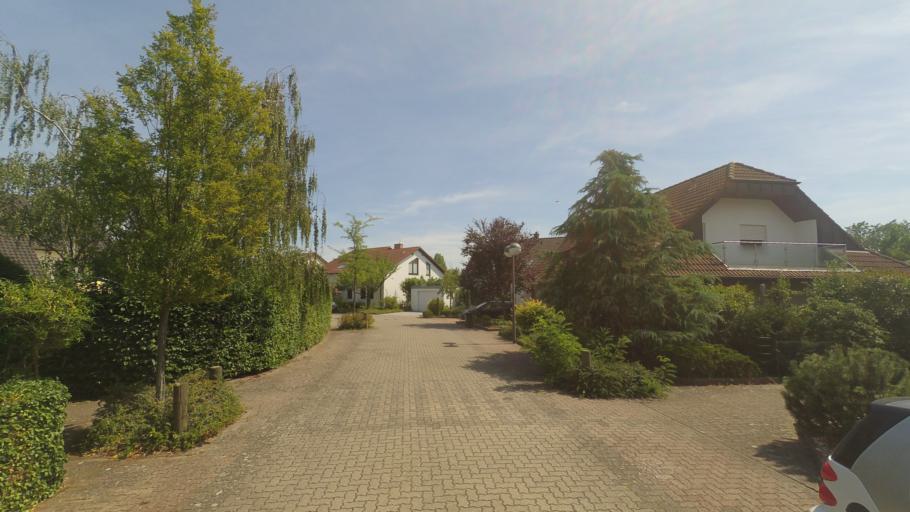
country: DE
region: Rheinland-Pfalz
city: Limburgerhof
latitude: 49.4232
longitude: 8.3759
